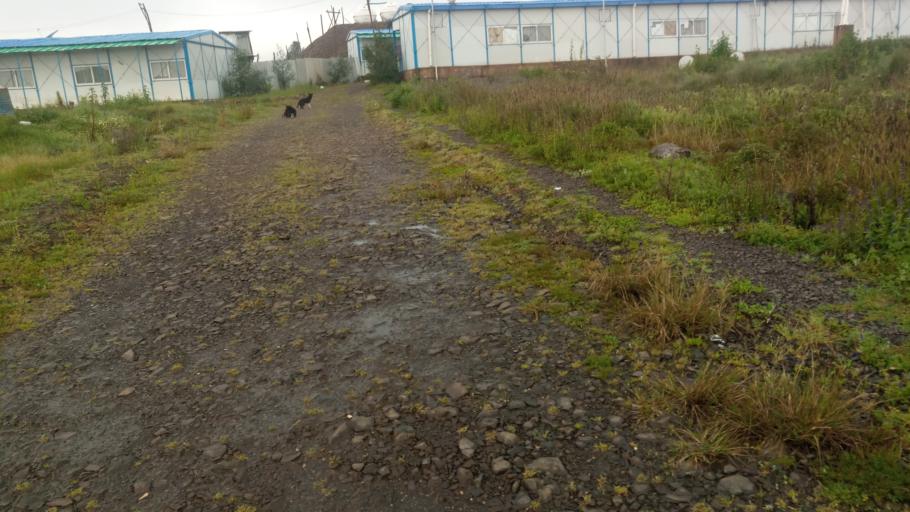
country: ET
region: Oromiya
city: Adis `Alem
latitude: 9.1725
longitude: 38.1273
